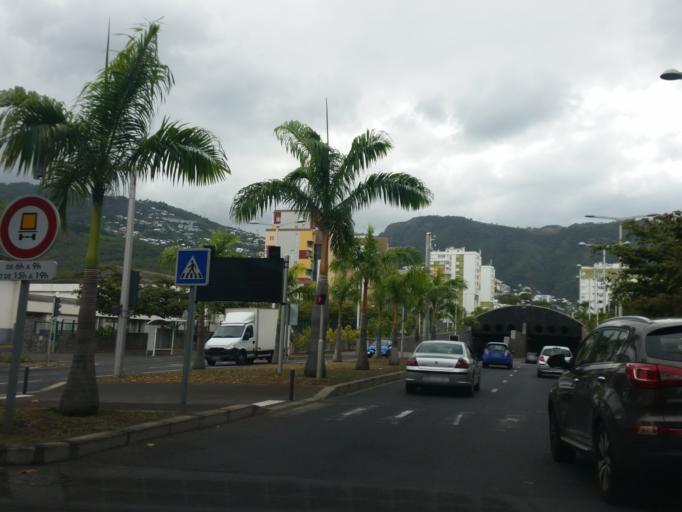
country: RE
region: Reunion
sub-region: Reunion
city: Saint-Denis
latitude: -20.8898
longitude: 55.4612
